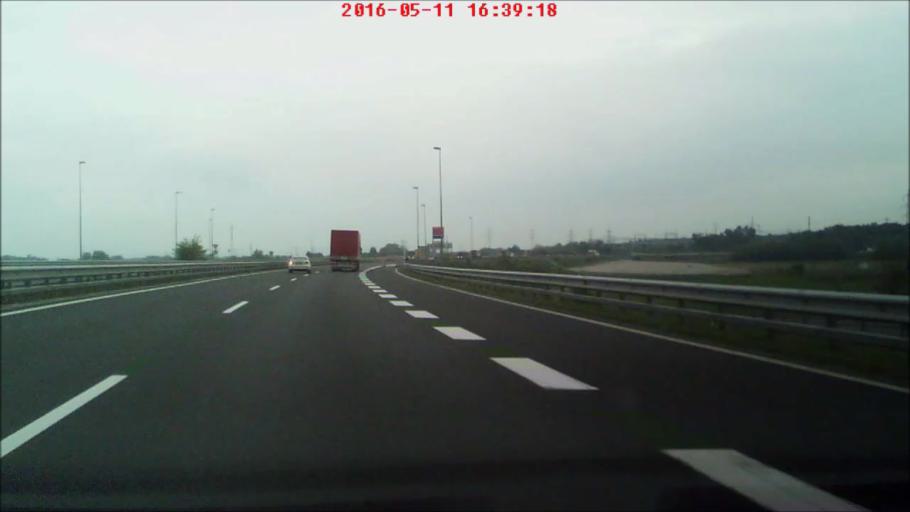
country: SI
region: Miklavz na Dravskem Polju
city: Miklavz na Dravskem Polju
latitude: 46.5381
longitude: 15.6988
